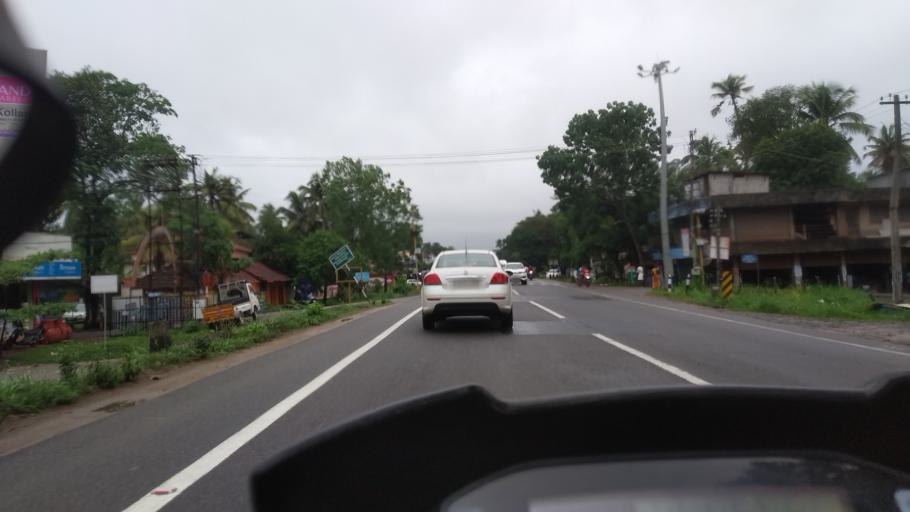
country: IN
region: Kerala
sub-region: Alappuzha
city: Mavelikara
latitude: 9.2737
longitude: 76.4599
